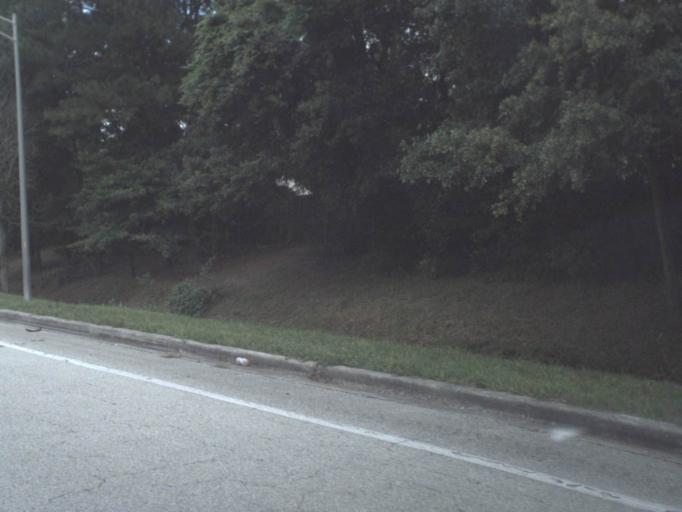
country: US
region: Florida
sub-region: Duval County
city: Jacksonville
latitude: 30.3048
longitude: -81.6148
